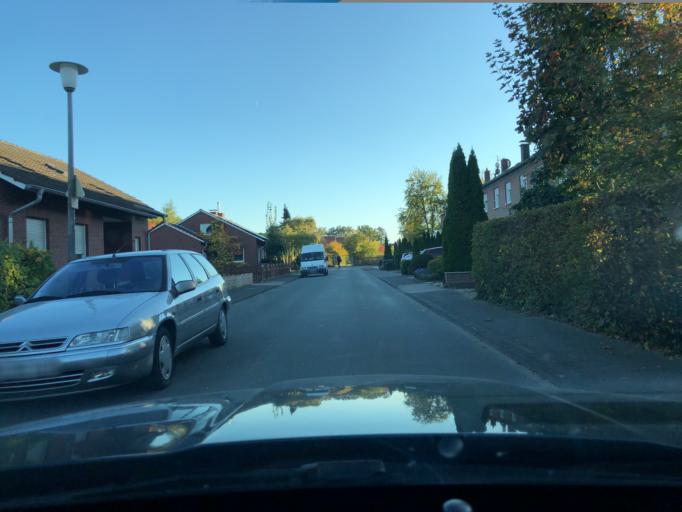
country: DE
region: North Rhine-Westphalia
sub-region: Regierungsbezirk Munster
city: Telgte
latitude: 52.0006
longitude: 7.7158
